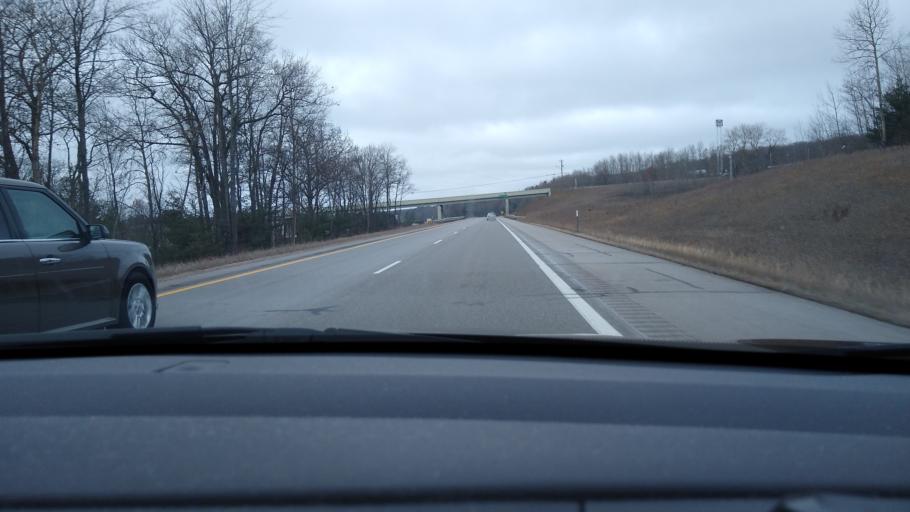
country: US
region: Michigan
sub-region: Otsego County
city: Gaylord
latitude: 44.8753
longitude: -84.6889
